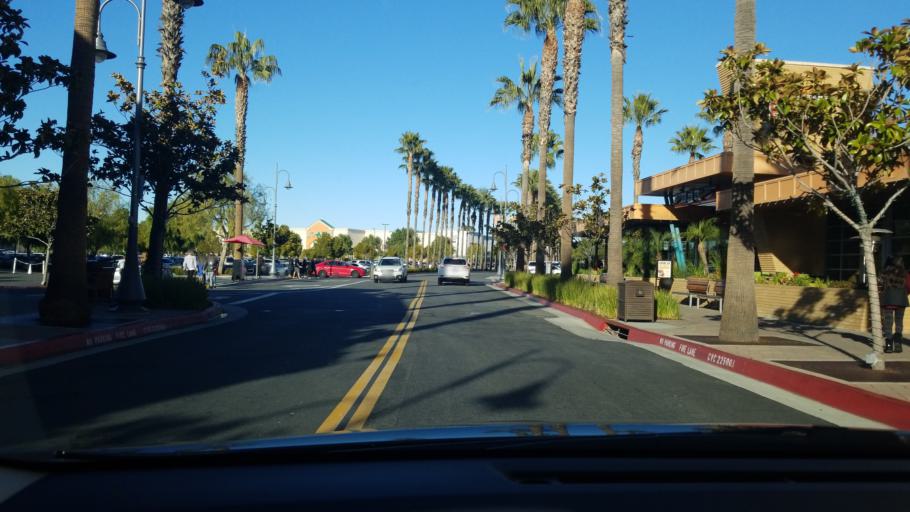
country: US
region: California
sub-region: Riverside County
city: Temecula
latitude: 33.5256
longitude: -117.1524
